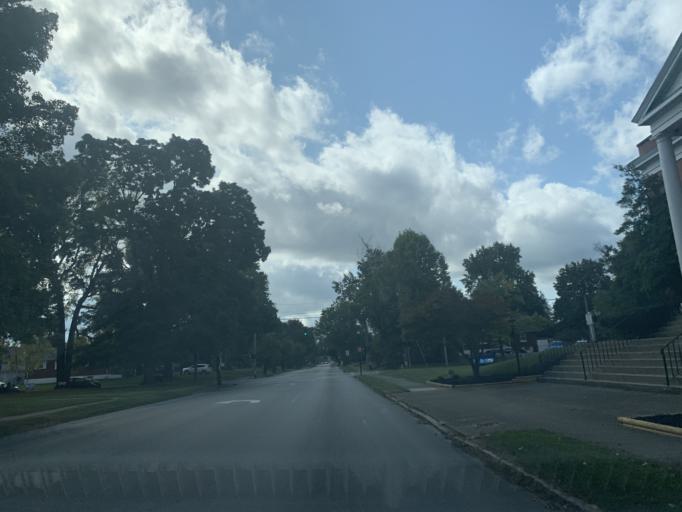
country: US
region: Kentucky
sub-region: Jefferson County
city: Audubon Park
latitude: 38.1845
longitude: -85.7657
